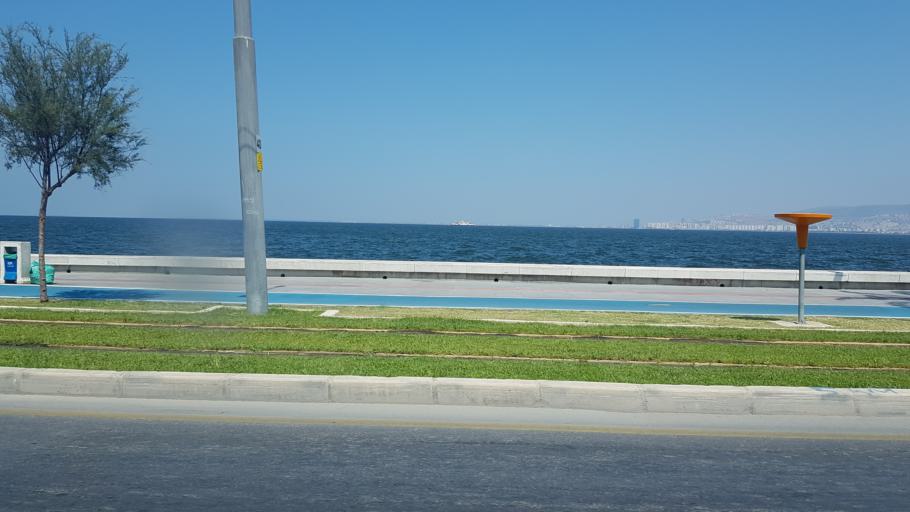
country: TR
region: Izmir
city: Izmir
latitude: 38.4035
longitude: 27.0960
